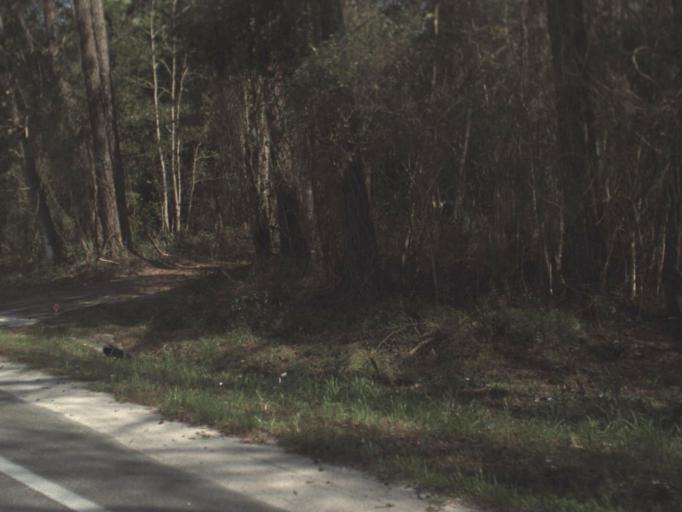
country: US
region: Florida
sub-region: Wakulla County
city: Crawfordville
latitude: 30.0680
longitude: -84.4592
